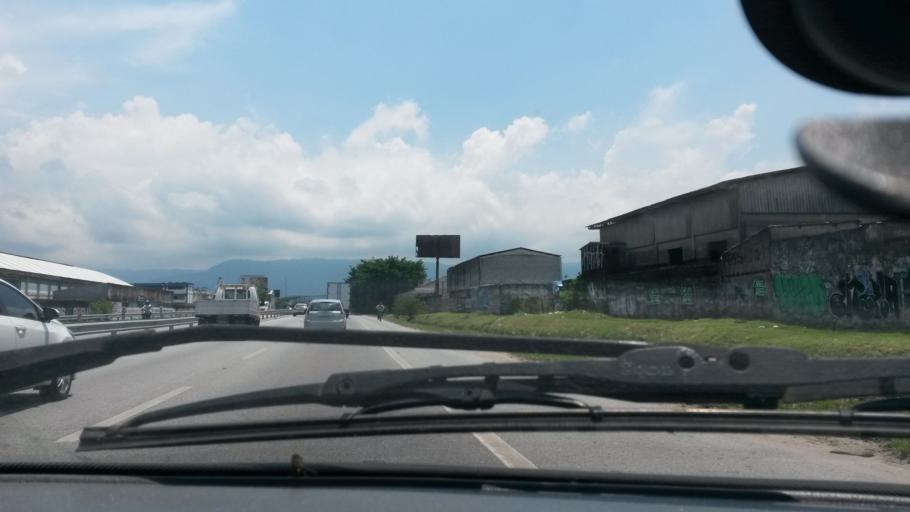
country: BR
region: Sao Paulo
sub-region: Sao Vicente
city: Sao Vicente
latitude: -23.9500
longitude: -46.4133
